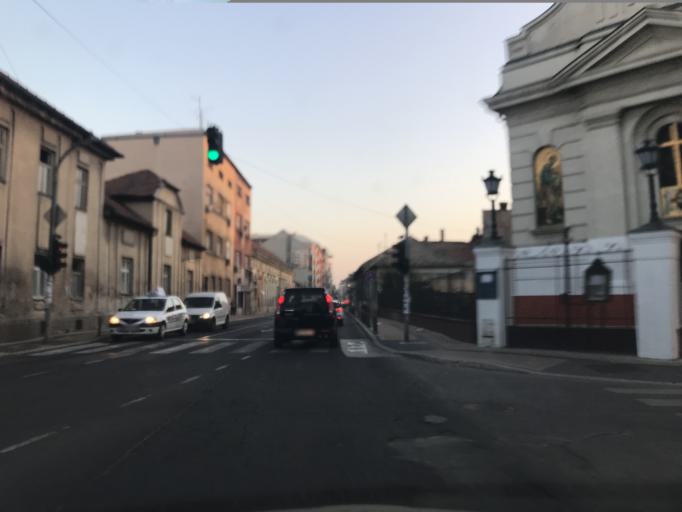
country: RS
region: Autonomna Pokrajina Vojvodina
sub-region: Juznobacki Okrug
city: Novi Sad
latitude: 45.2579
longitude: 19.8420
